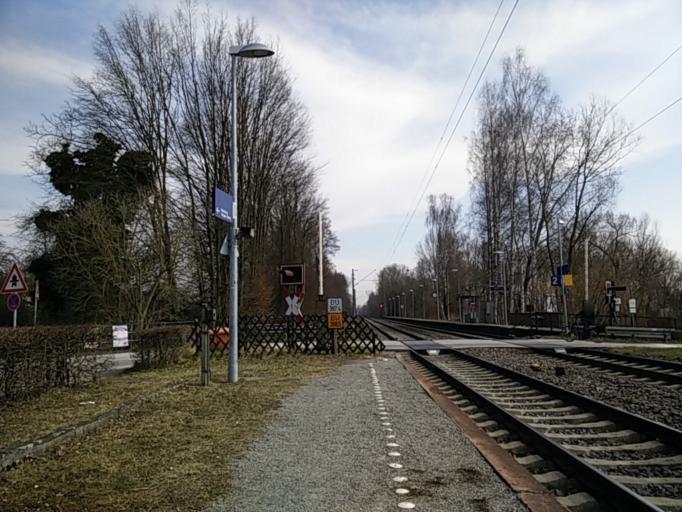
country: DE
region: Baden-Wuerttemberg
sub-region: Freiburg Region
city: Radolfzell am Bodensee
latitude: 47.7392
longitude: 9.0032
